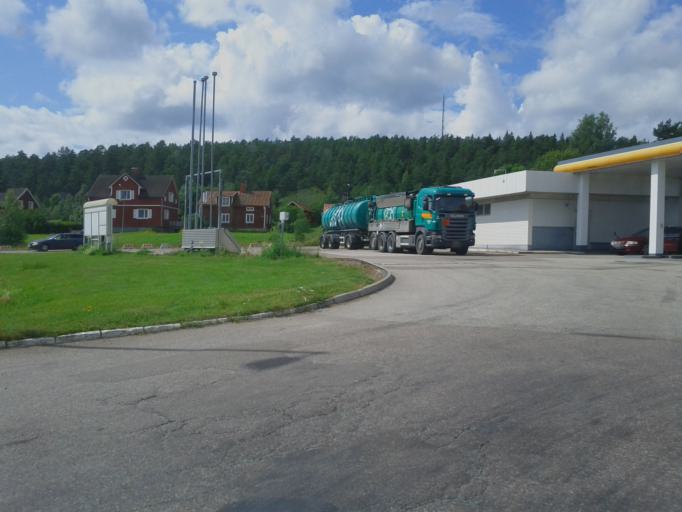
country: SE
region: Dalarna
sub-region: Hedemora Kommun
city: Hedemora
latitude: 60.2964
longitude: 15.9786
